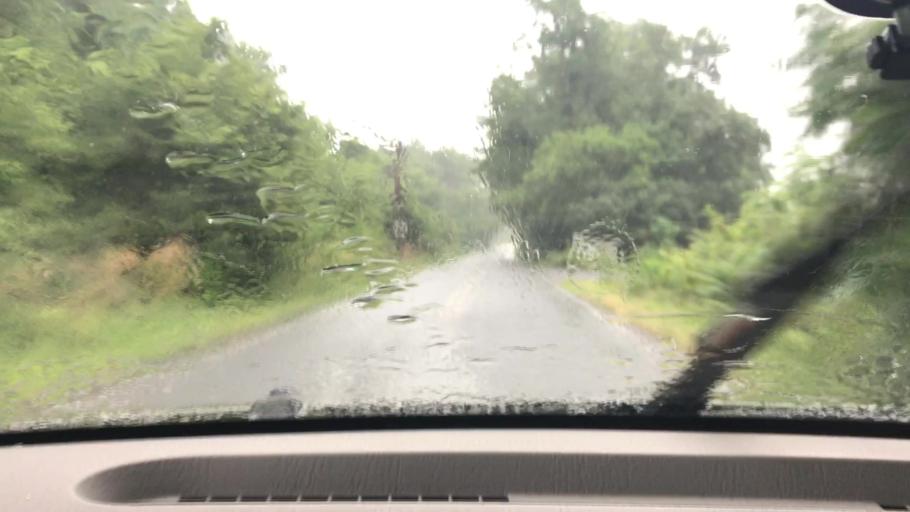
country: US
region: Pennsylvania
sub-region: Lancaster County
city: Rheems
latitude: 40.1306
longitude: -76.5822
